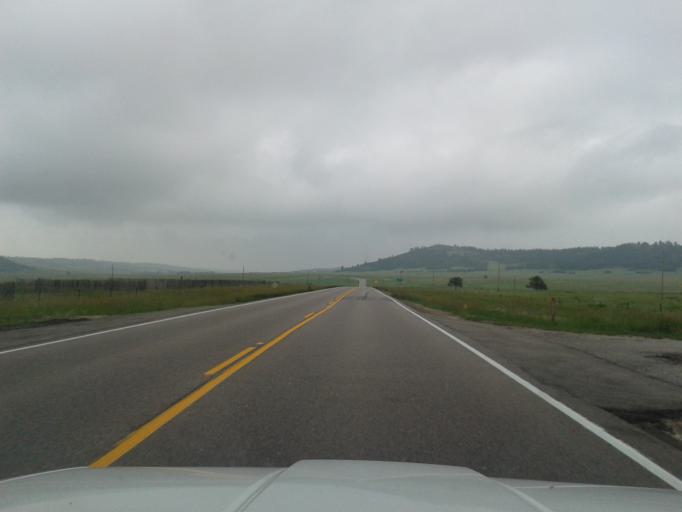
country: US
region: Colorado
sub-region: El Paso County
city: Woodmoor
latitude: 39.1487
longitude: -104.7585
